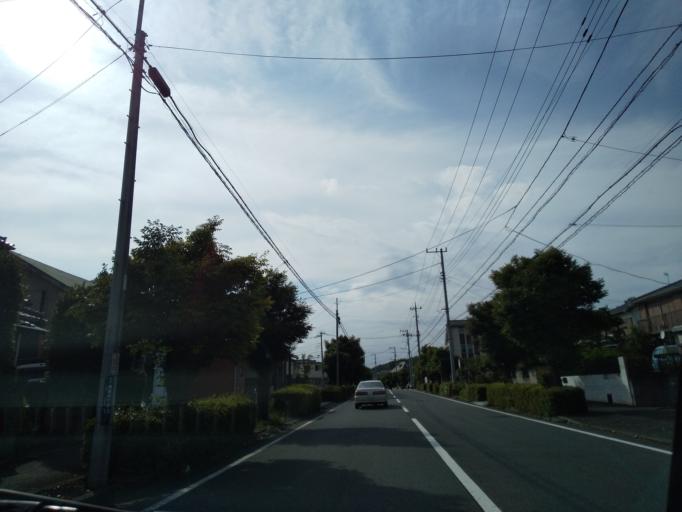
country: JP
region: Kanagawa
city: Zama
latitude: 35.4932
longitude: 139.3248
